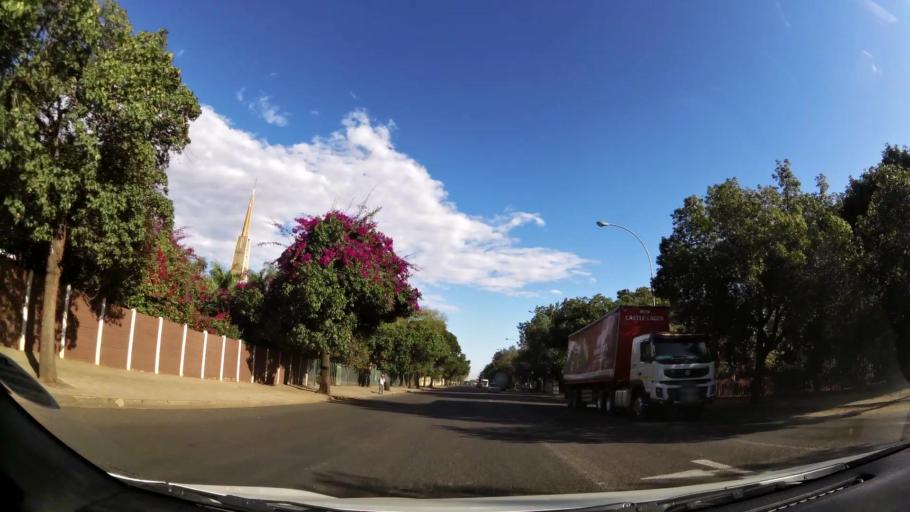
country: ZA
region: Limpopo
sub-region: Waterberg District Municipality
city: Mokopane
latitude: -24.1918
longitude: 29.0100
